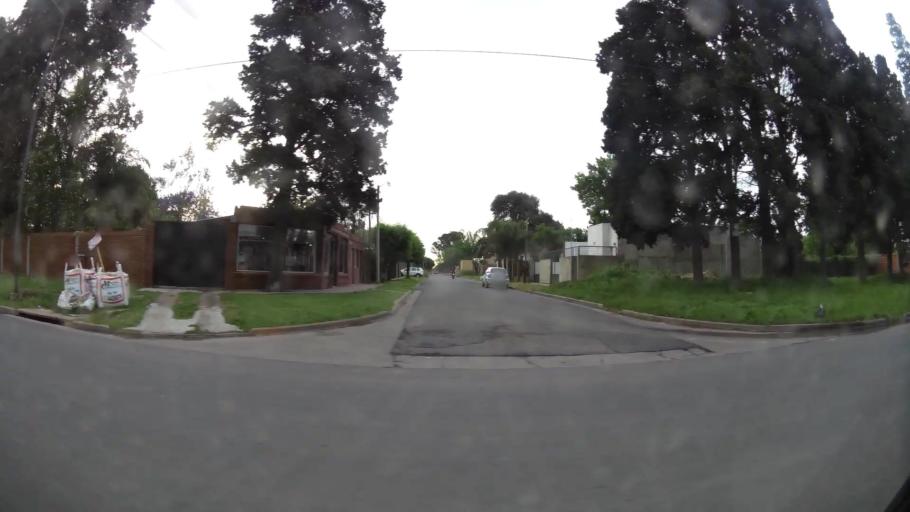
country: AR
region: Buenos Aires
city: San Nicolas de los Arroyos
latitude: -33.3535
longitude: -60.1999
